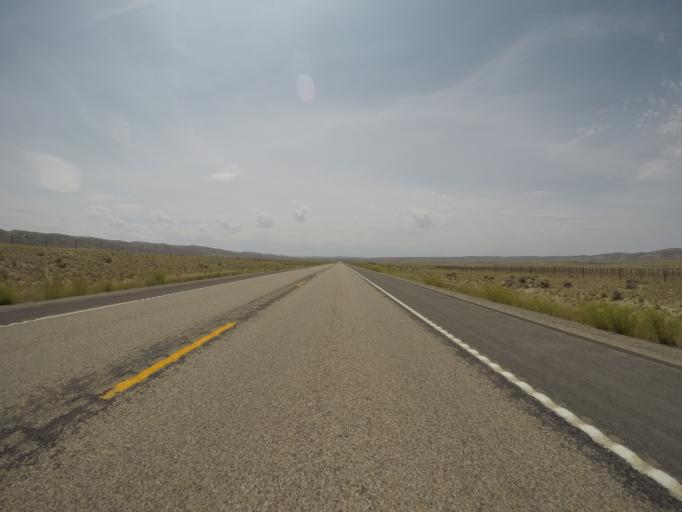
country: US
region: Wyoming
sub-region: Lincoln County
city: Kemmerer
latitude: 41.6602
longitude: -110.5701
